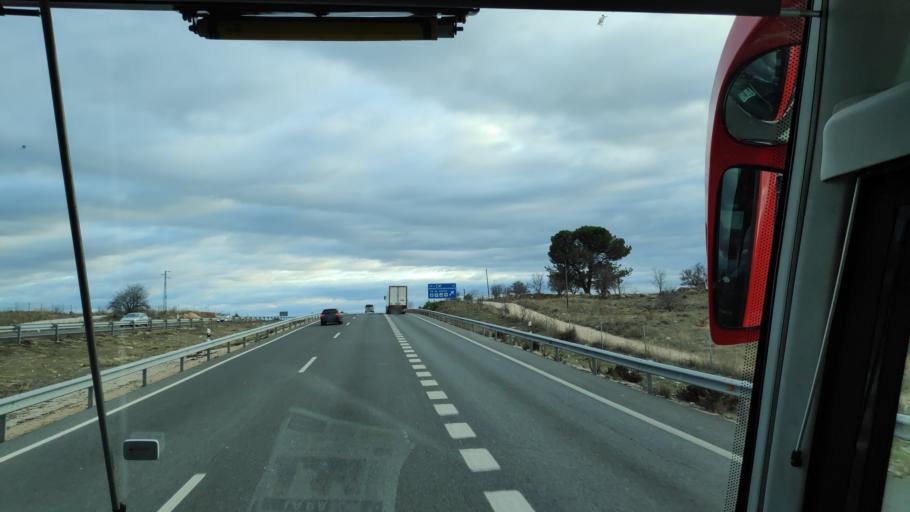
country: ES
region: Madrid
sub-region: Provincia de Madrid
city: Villarejo de Salvanes
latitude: 40.1832
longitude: -3.2975
